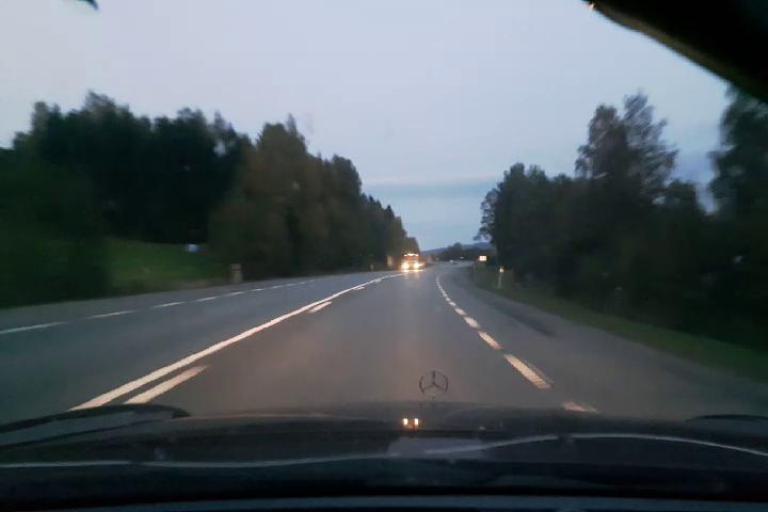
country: SE
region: Vaesternorrland
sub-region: Kramfors Kommun
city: Nordingra
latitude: 63.0072
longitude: 18.2824
